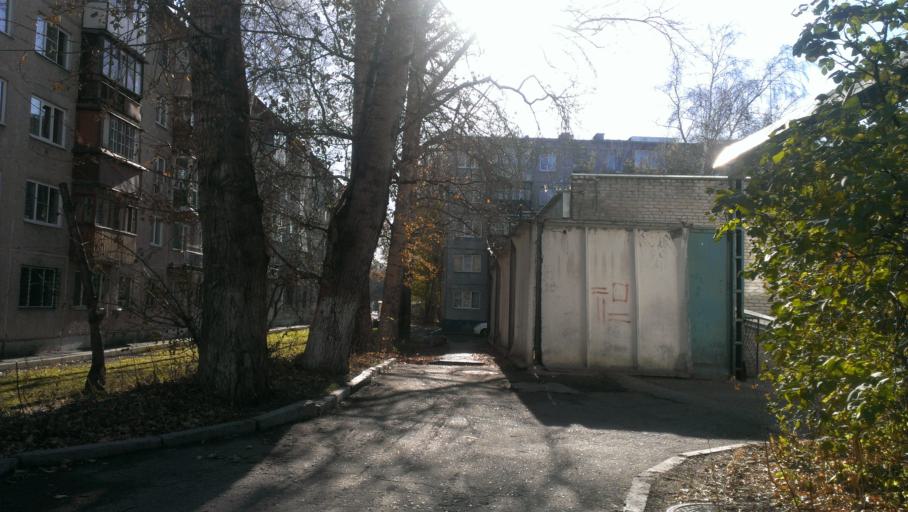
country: RU
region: Altai Krai
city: Novosilikatnyy
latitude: 53.3491
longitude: 83.6807
